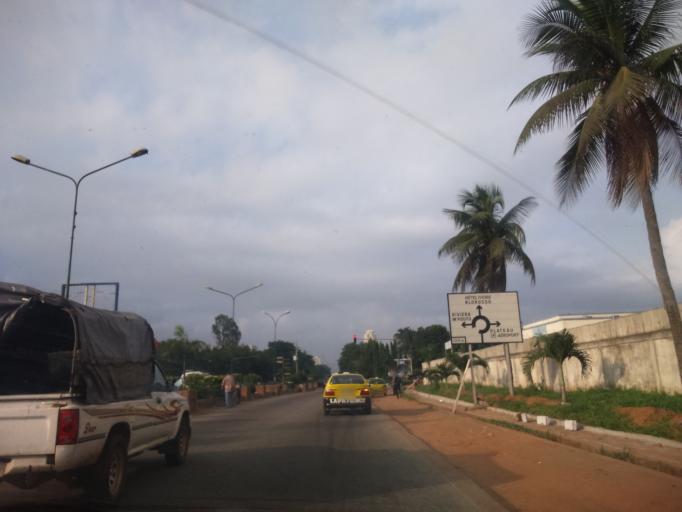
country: CI
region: Lagunes
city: Abidjan
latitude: 5.3369
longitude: -4.0039
